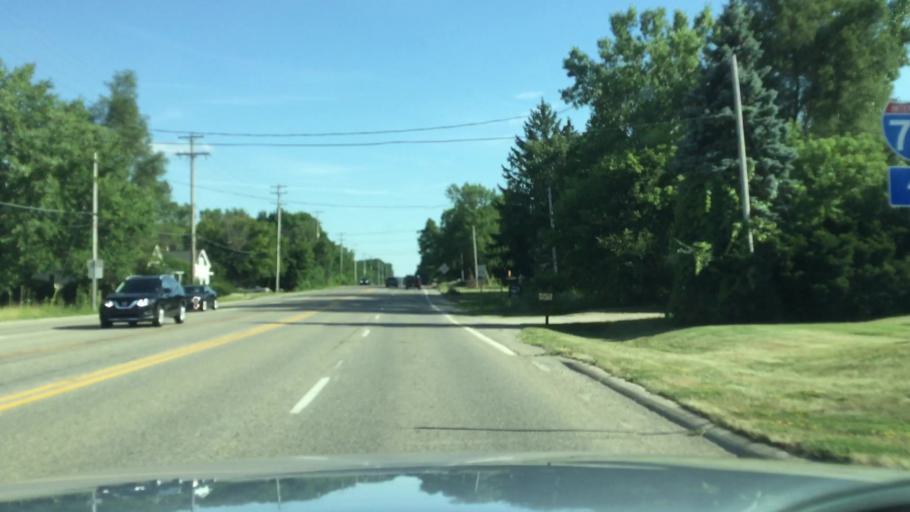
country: US
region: Michigan
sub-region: Genesee County
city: Grand Blanc
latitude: 42.8868
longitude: -83.5991
